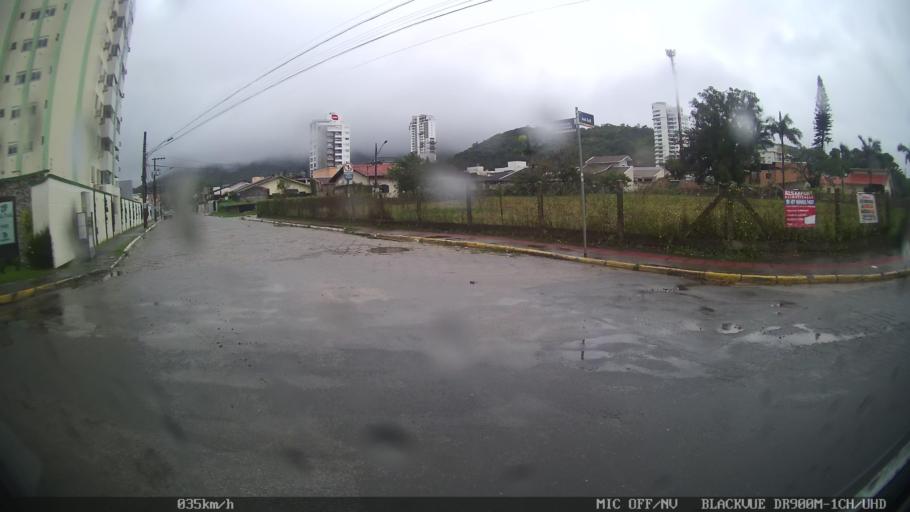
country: BR
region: Santa Catarina
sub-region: Itajai
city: Itajai
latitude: -26.9235
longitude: -48.6821
